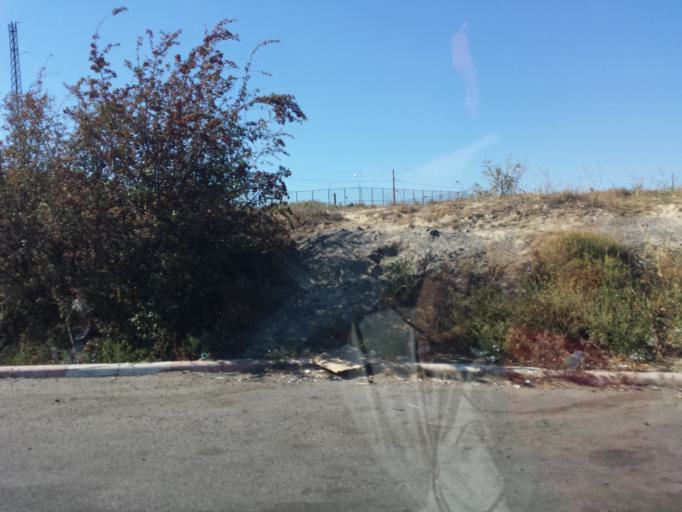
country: RO
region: Tulcea
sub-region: Municipiul Tulcea
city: Tulcea
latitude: 45.1619
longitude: 28.7880
